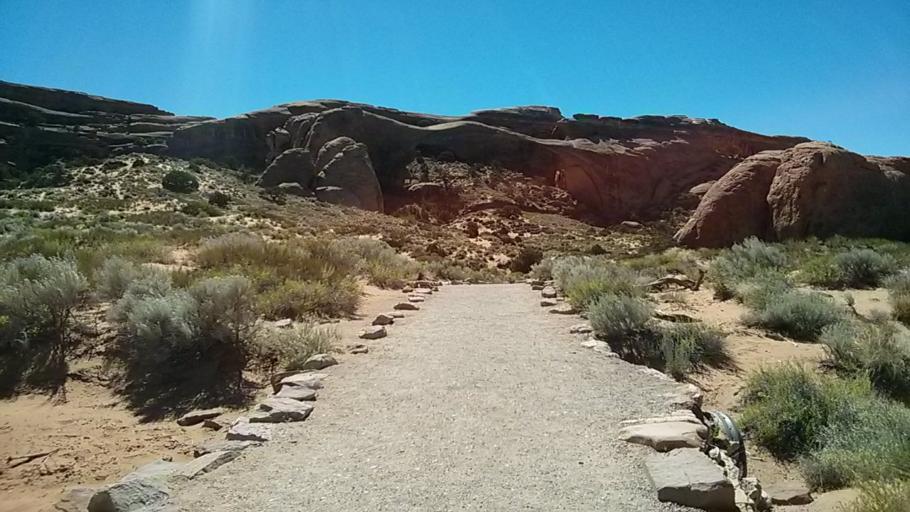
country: US
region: Utah
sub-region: Grand County
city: Moab
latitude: 38.7904
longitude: -109.6035
